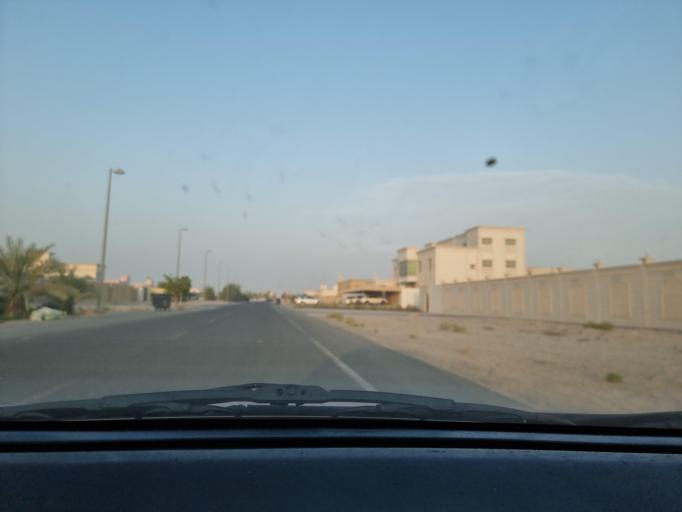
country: AE
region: Abu Dhabi
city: Abu Dhabi
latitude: 24.3814
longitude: 54.7020
